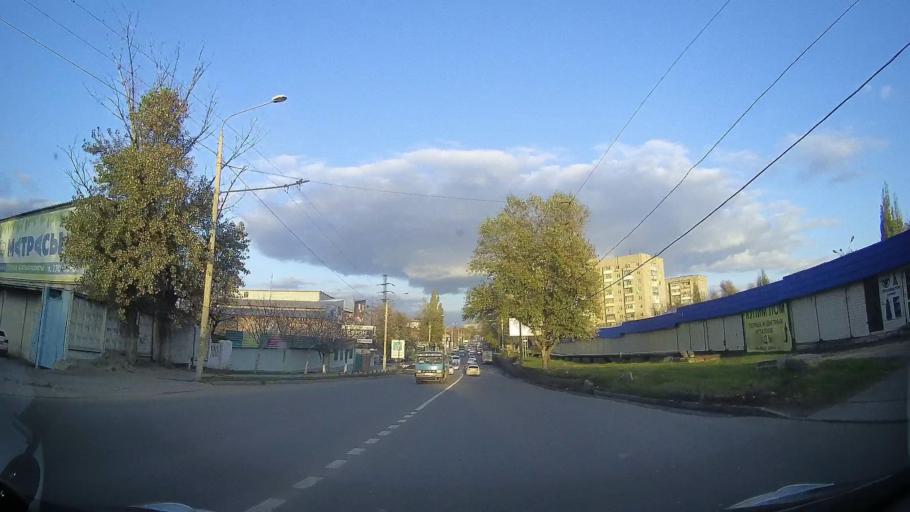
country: RU
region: Rostov
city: Imeni Chkalova
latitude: 47.2633
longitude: 39.7737
